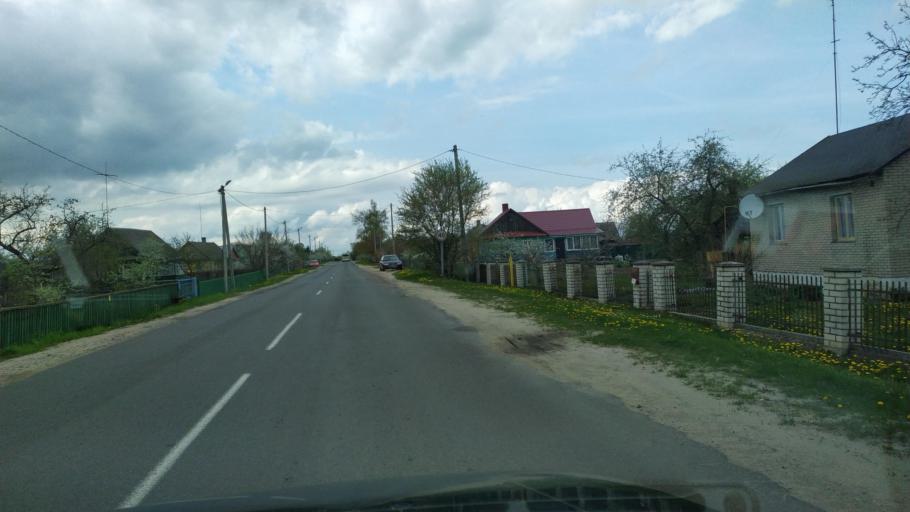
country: BY
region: Brest
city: Pruzhany
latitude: 52.5701
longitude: 24.4169
